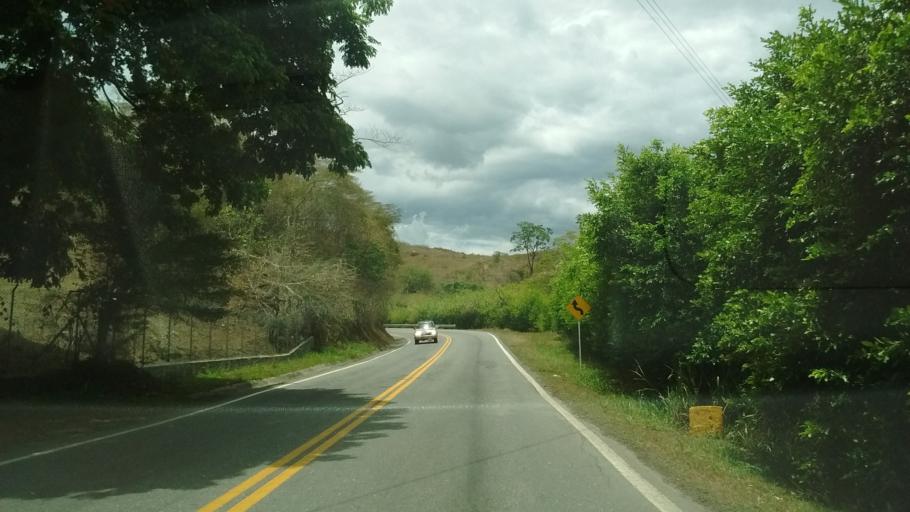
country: CO
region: Cauca
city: La Sierra
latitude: 2.2066
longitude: -76.8074
